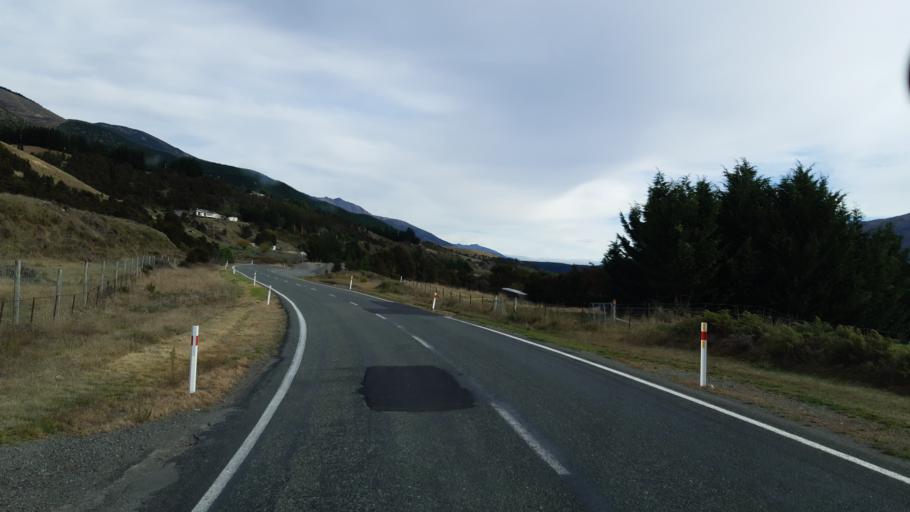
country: NZ
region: Tasman
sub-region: Tasman District
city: Wakefield
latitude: -41.6888
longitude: 173.1536
